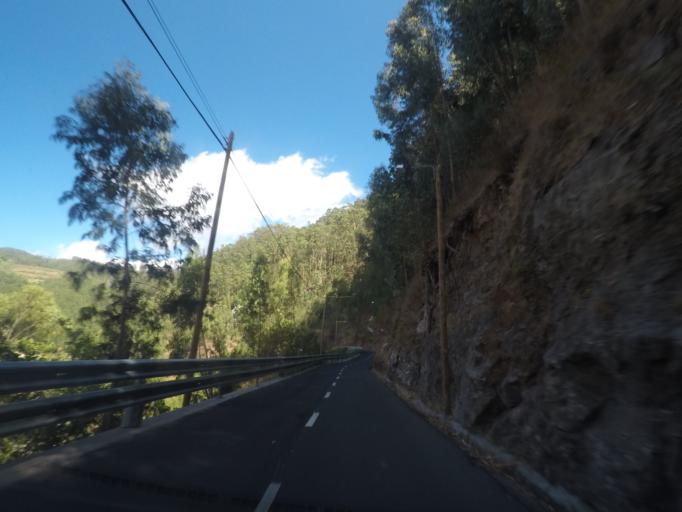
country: PT
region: Madeira
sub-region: Ribeira Brava
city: Campanario
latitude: 32.6874
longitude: -17.0328
